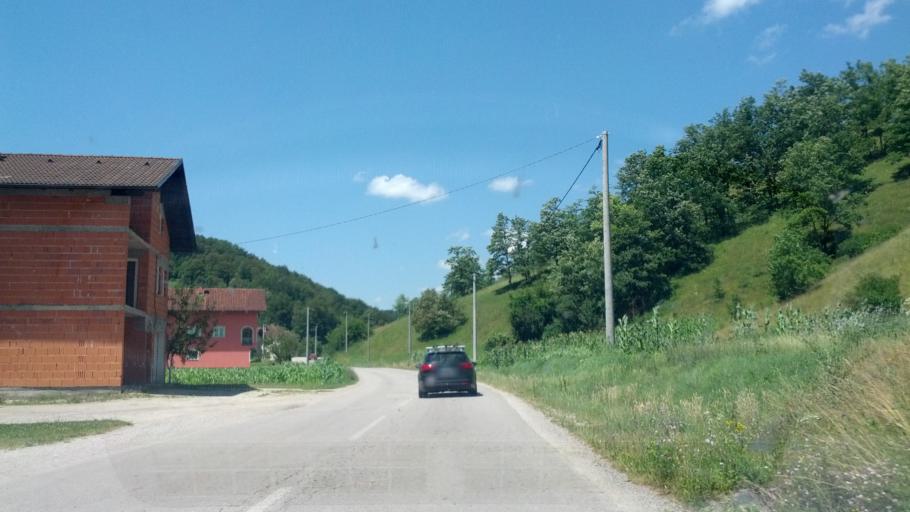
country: BA
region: Federation of Bosnia and Herzegovina
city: Jezerski
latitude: 45.0220
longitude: 16.0866
